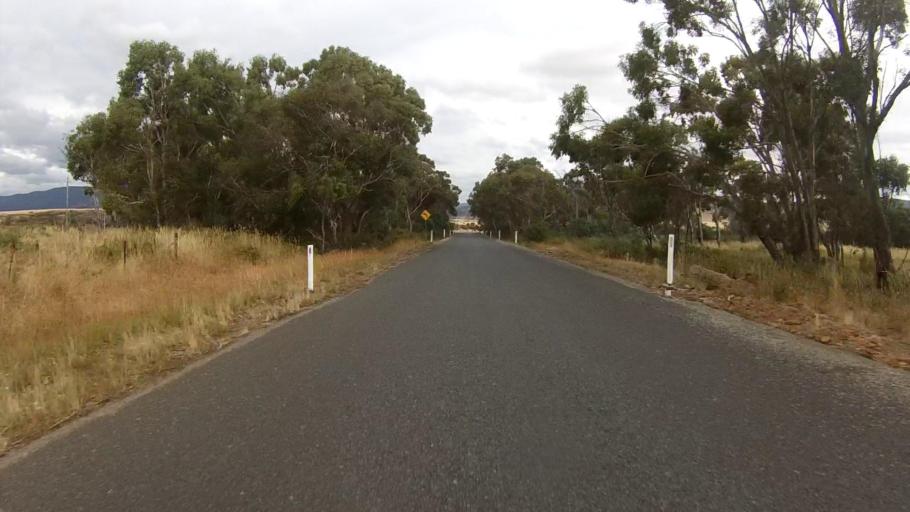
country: AU
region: Tasmania
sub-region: Northern Midlands
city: Evandale
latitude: -41.8141
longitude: 147.7539
